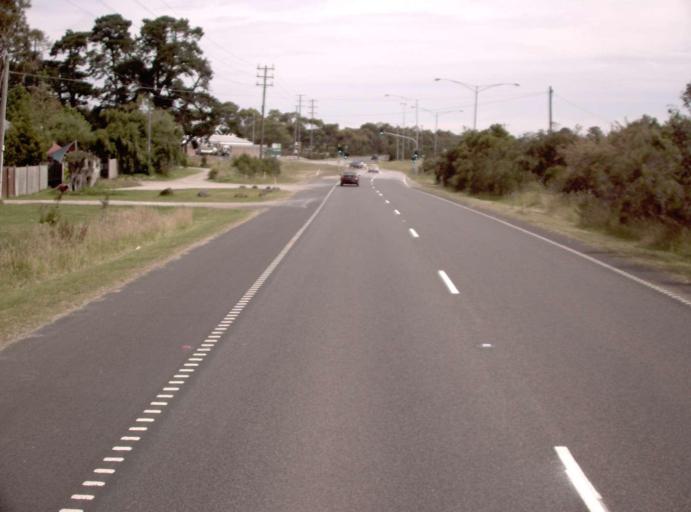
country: AU
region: Victoria
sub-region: Mornington Peninsula
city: Moorooduc
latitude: -38.2122
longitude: 145.1101
